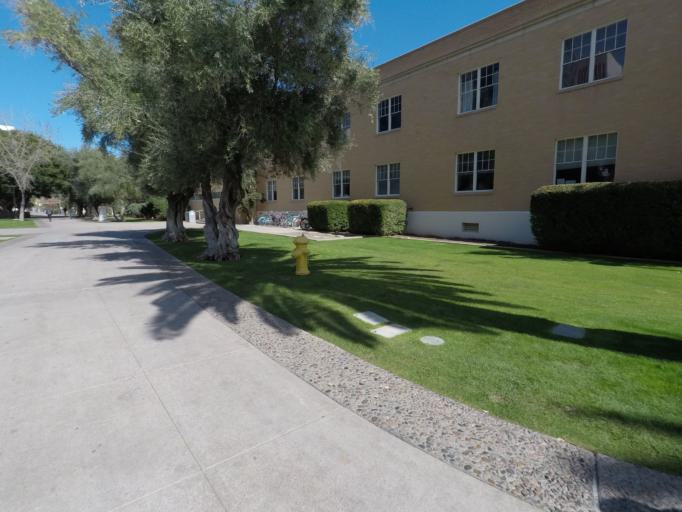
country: US
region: Arizona
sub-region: Maricopa County
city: Tempe Junction
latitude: 33.4191
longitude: -111.9365
